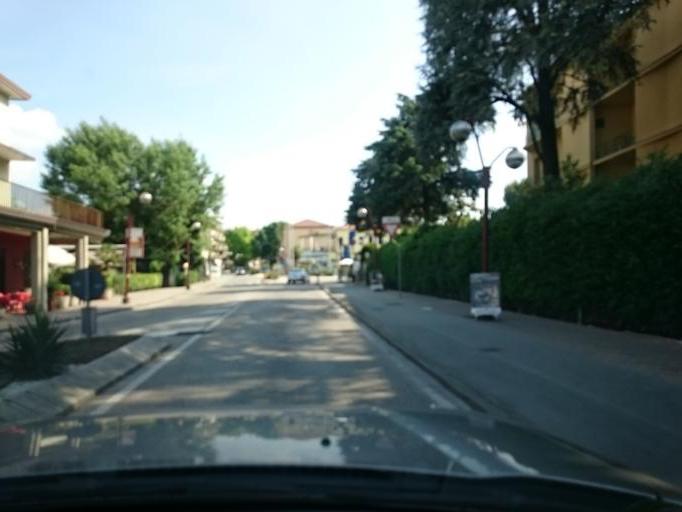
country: IT
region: Veneto
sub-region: Provincia di Padova
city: Montegrotto Terme
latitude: 45.3343
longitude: 11.7836
